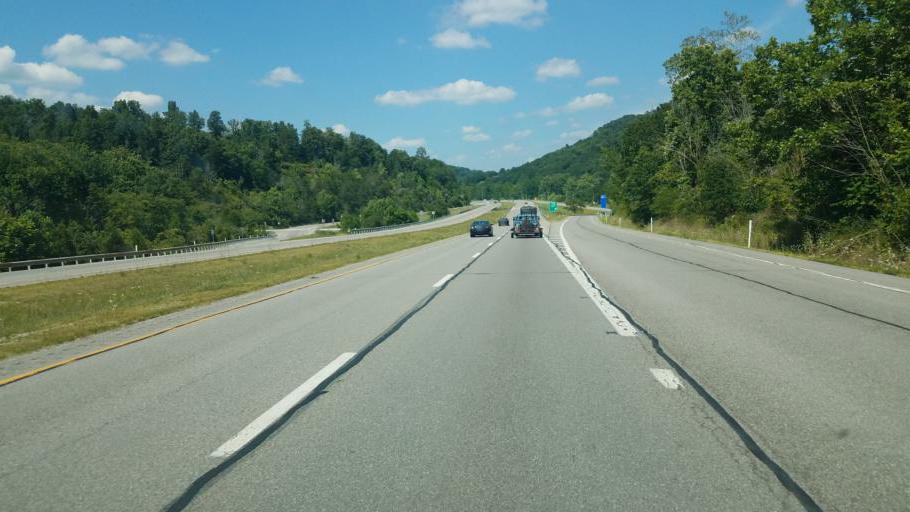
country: US
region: West Virginia
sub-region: Kanawha County
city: Sissonville
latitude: 38.5420
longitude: -81.6393
